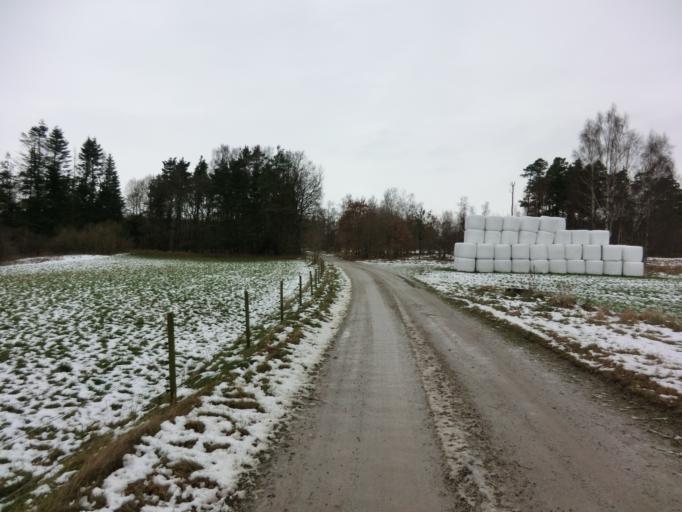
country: SE
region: Skane
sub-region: Hoors Kommun
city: Loberod
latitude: 55.7367
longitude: 13.3971
